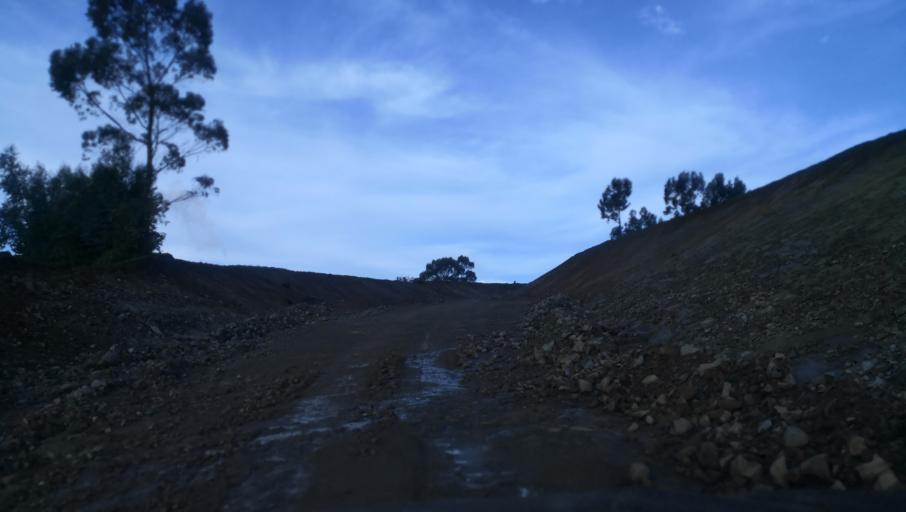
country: ET
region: Southern Nations, Nationalities, and People's Region
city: Butajira
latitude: 8.3986
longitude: 38.3174
